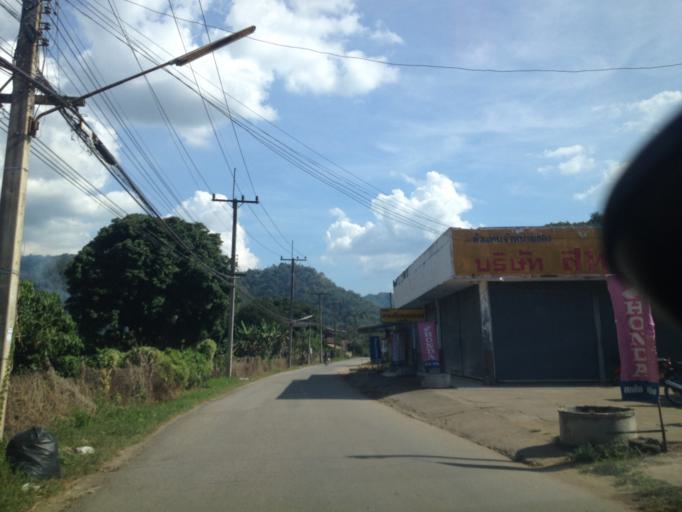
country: TH
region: Chiang Mai
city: Samoeng
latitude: 18.8634
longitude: 98.7240
